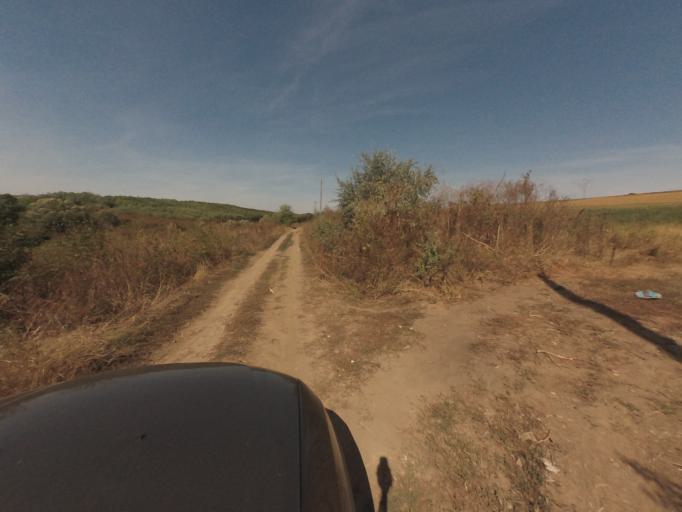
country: RO
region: Vaslui
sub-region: Comuna Costesti
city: Costesti
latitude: 46.5152
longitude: 27.7432
